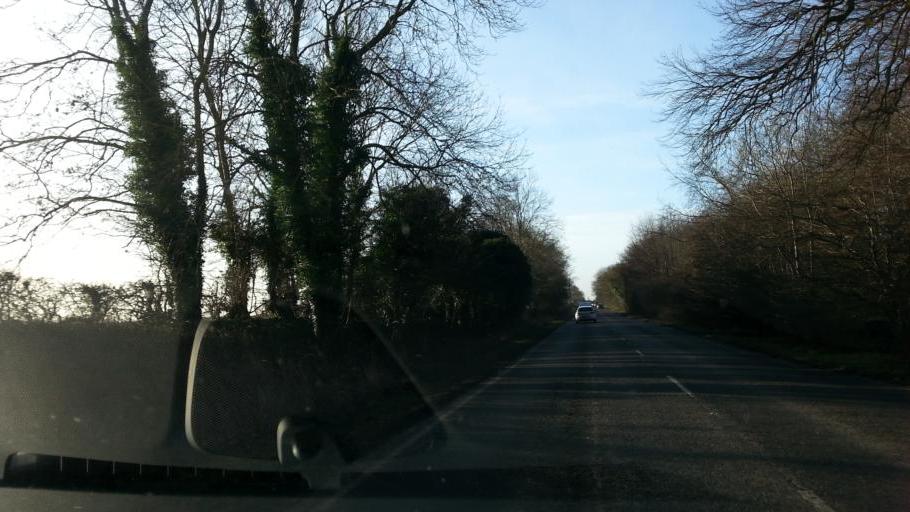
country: GB
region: England
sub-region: Lincolnshire
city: Grantham
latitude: 52.9083
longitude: -0.5842
